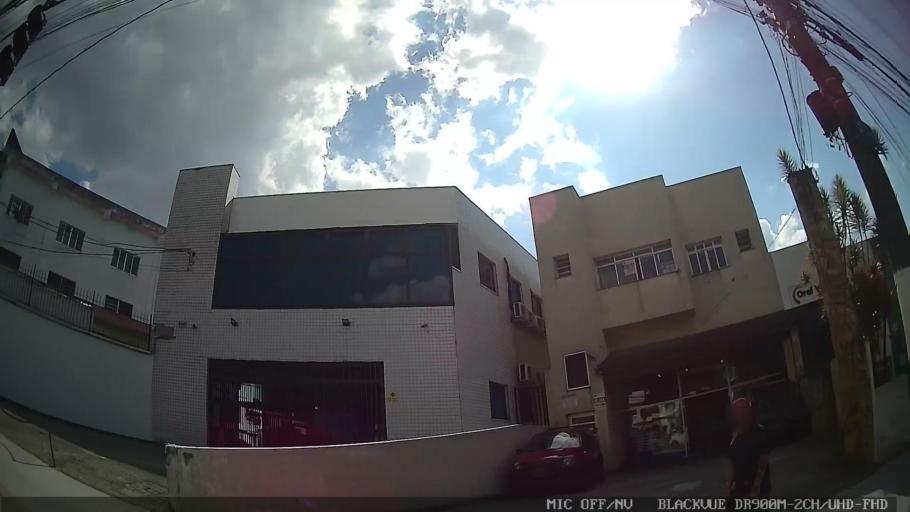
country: BR
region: Sao Paulo
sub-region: Ferraz De Vasconcelos
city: Ferraz de Vasconcelos
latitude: -23.4972
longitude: -46.4415
